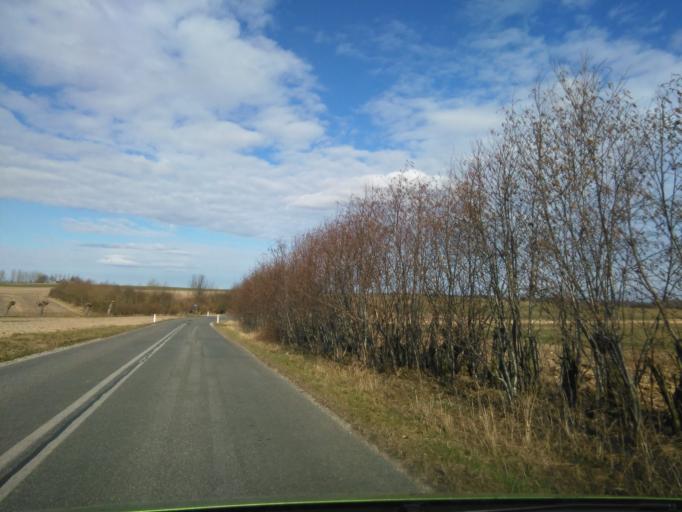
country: DK
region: Central Jutland
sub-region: Odder Kommune
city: Odder
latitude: 55.9228
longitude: 10.0546
